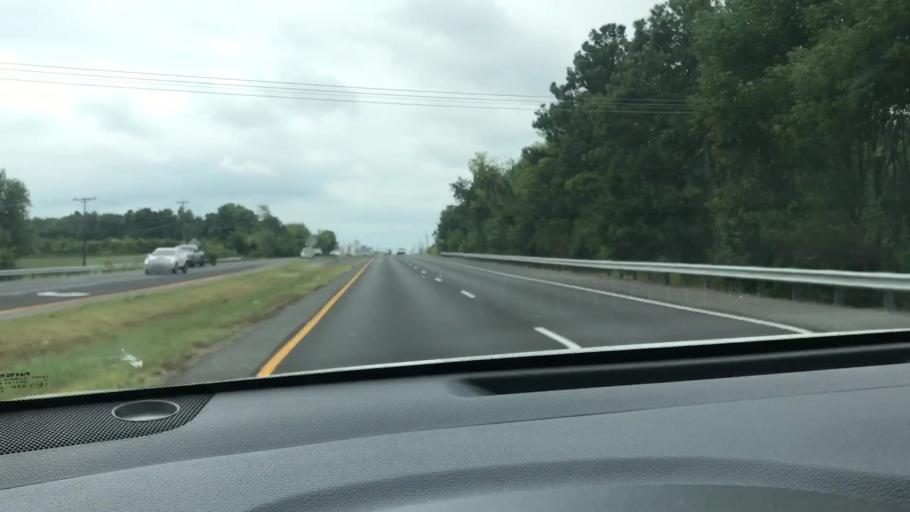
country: US
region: Kentucky
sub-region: Calloway County
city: Murray
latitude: 36.6458
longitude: -88.3082
